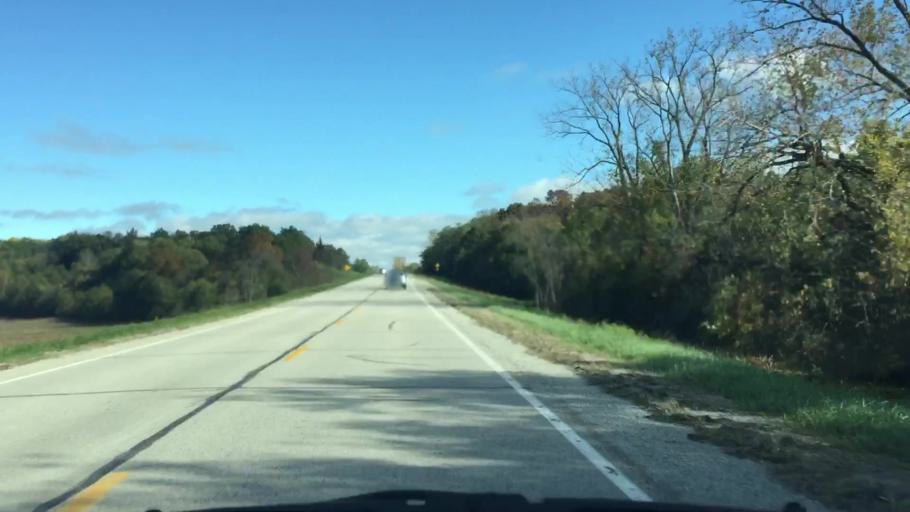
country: US
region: Iowa
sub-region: Decatur County
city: Leon
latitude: 40.6543
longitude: -93.7991
